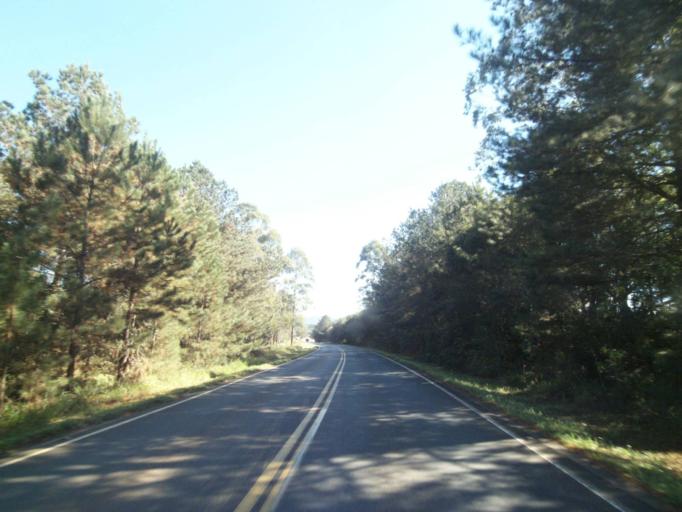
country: BR
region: Parana
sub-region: Tibagi
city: Tibagi
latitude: -24.4845
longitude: -50.4737
